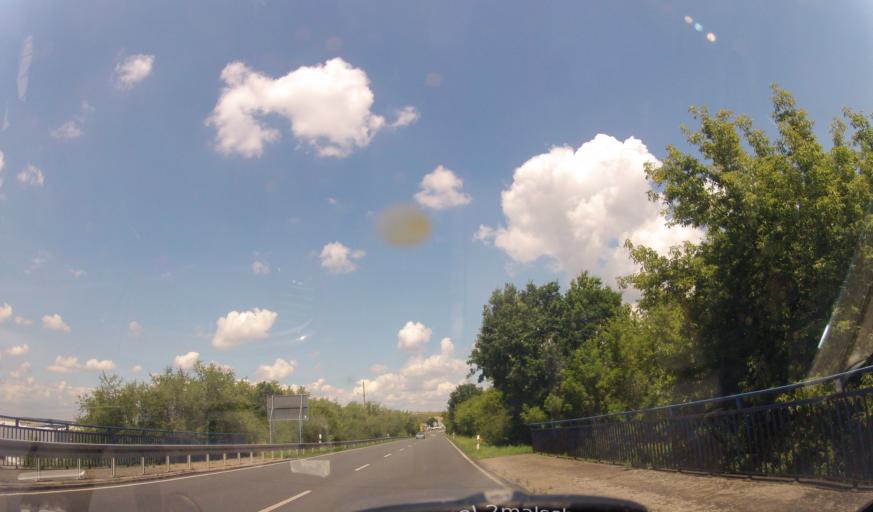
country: DE
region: Saxony
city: Zinna
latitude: 51.5529
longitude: 12.9657
